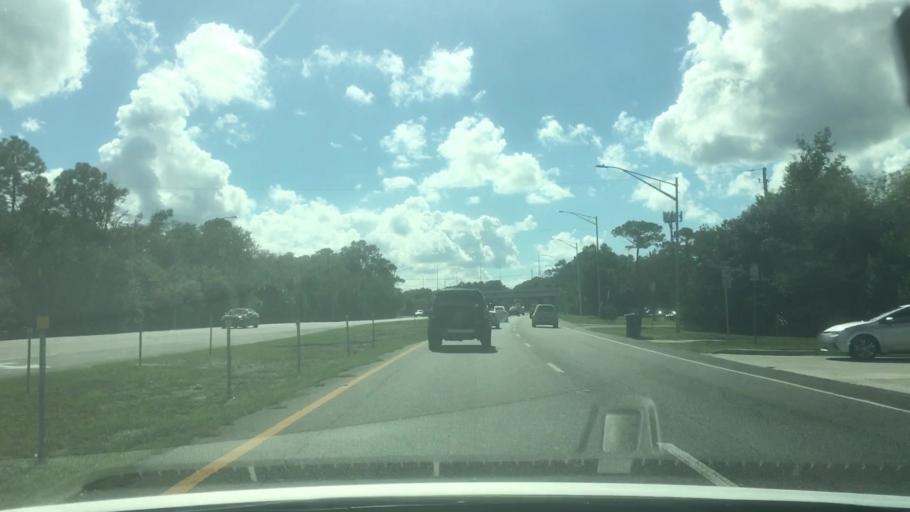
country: US
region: Florida
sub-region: Duval County
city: Atlantic Beach
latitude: 30.3200
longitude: -81.5236
